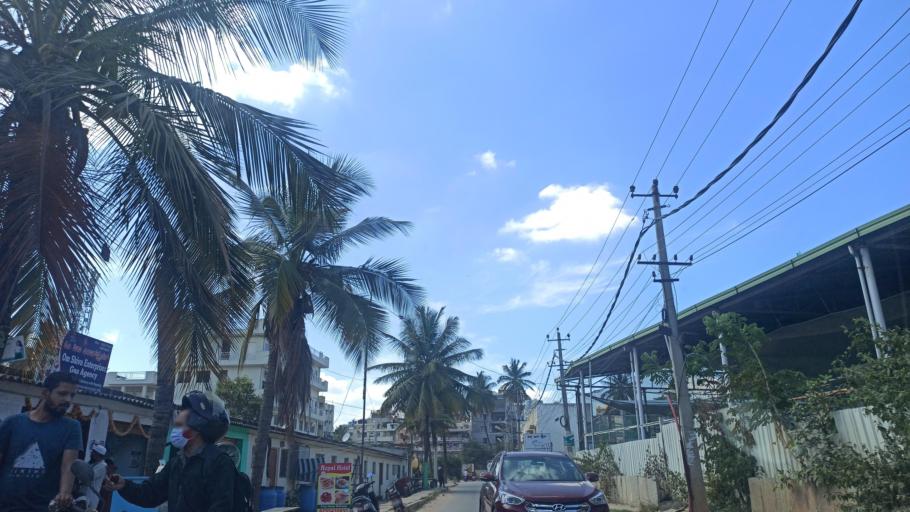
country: IN
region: Karnataka
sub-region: Bangalore Urban
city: Bangalore
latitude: 12.9300
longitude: 77.6801
